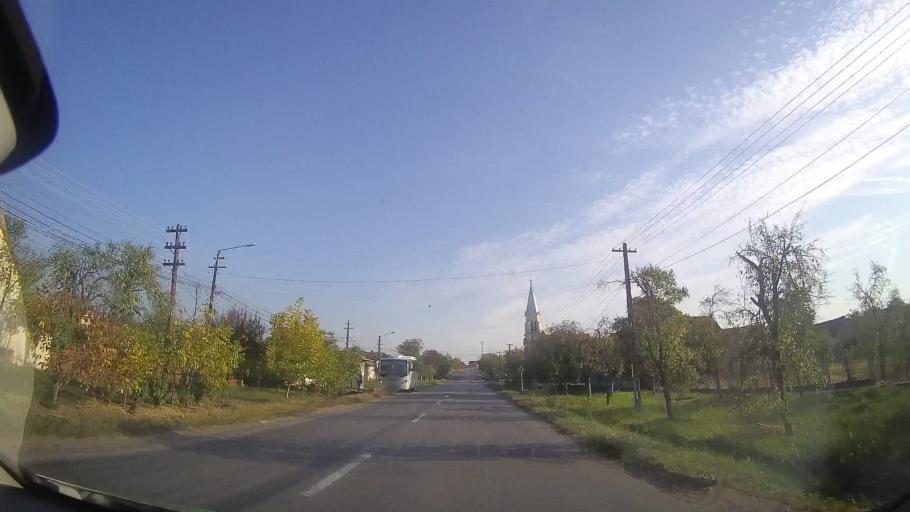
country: RO
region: Timis
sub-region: Comuna Fibis
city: Fibis
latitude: 45.9781
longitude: 21.4258
